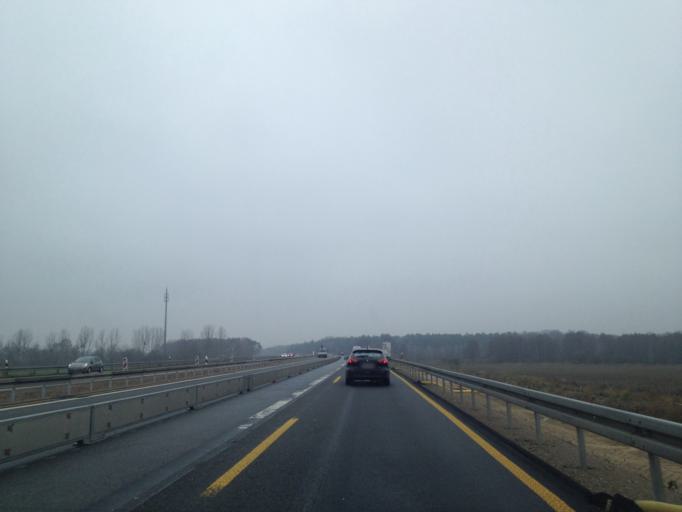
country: DE
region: Berlin
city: Blankenfelde
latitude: 52.6671
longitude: 13.4058
